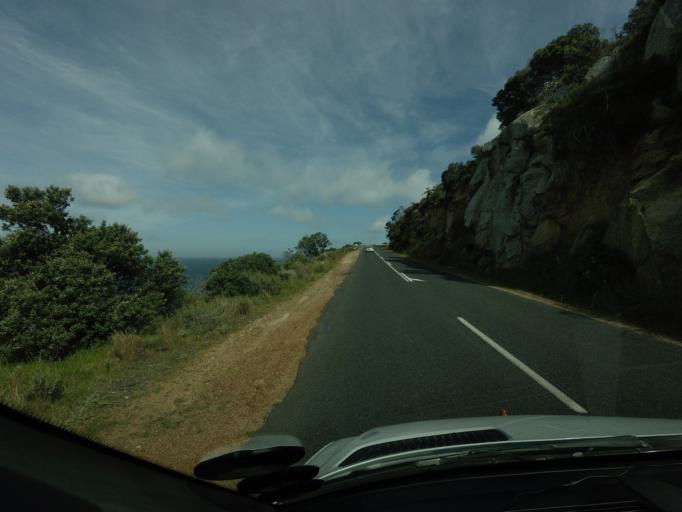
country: ZA
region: Western Cape
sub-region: City of Cape Town
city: Retreat
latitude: -34.2435
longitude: 18.4739
